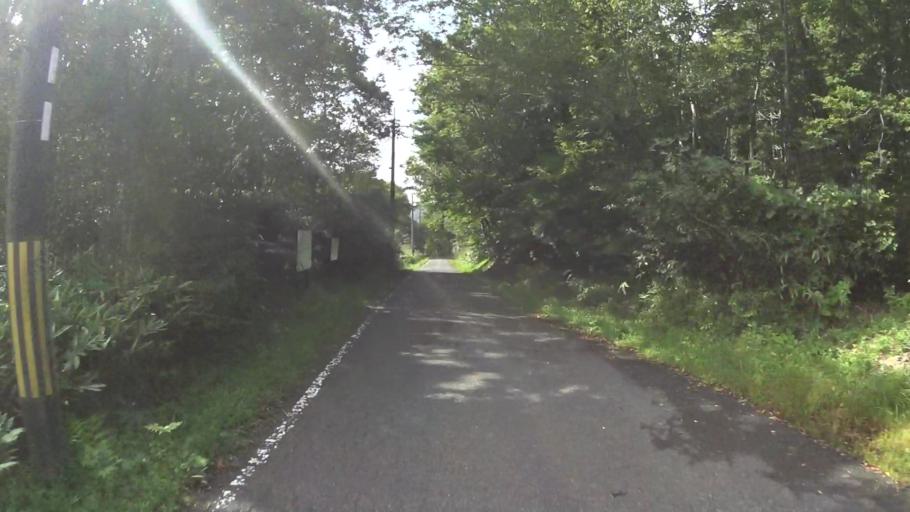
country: JP
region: Kyoto
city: Miyazu
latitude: 35.6508
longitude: 135.1805
